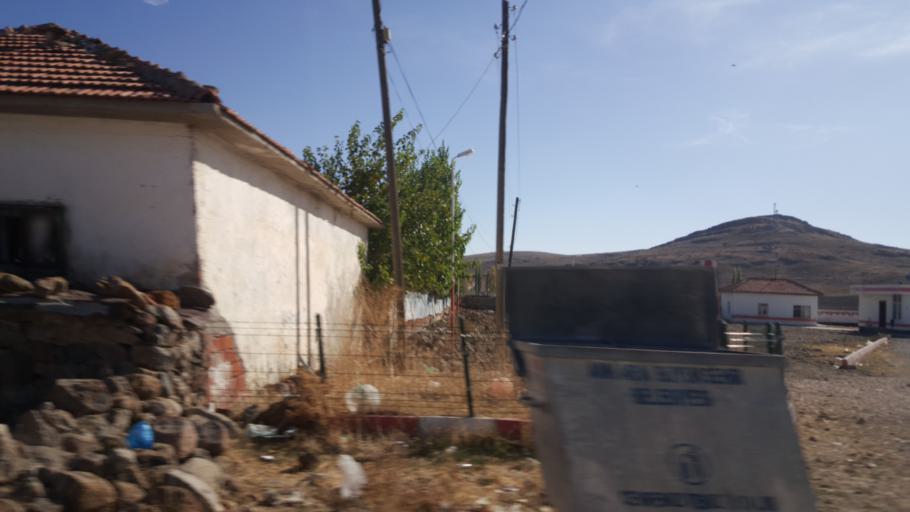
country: TR
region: Ankara
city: Yenice
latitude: 39.2739
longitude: 32.6727
